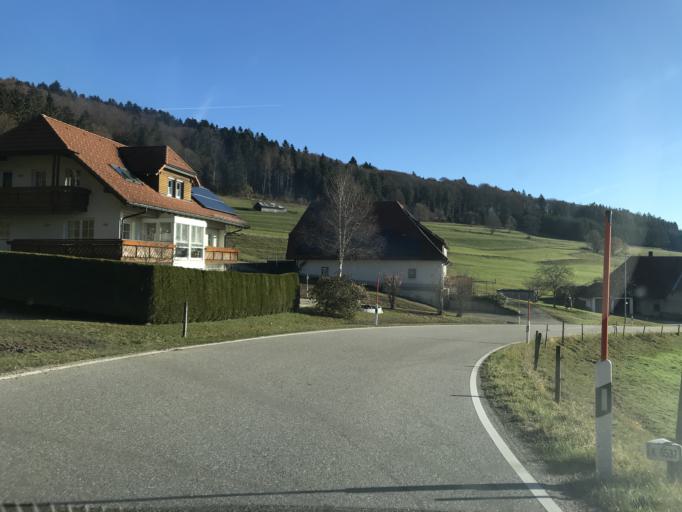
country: DE
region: Baden-Wuerttemberg
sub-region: Freiburg Region
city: Rickenbach
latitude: 47.6410
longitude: 7.9692
